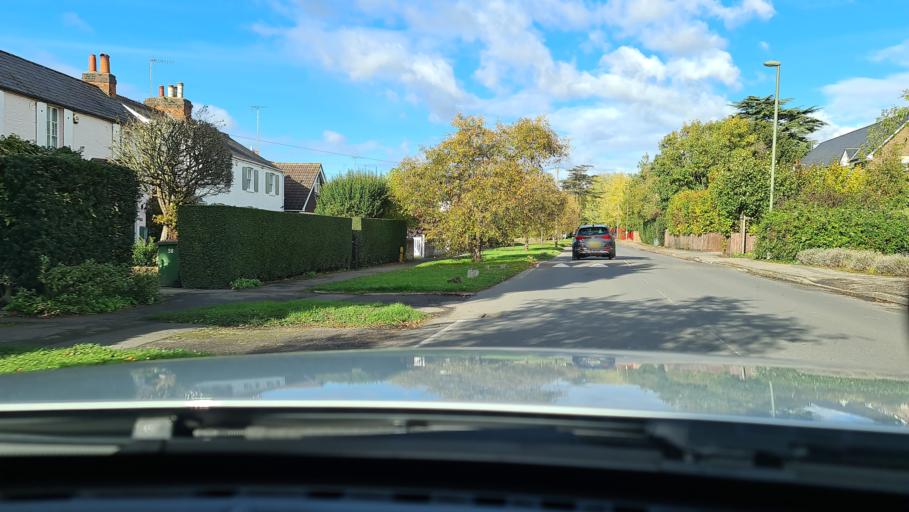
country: GB
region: England
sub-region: Surrey
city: Esher
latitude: 51.3638
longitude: -0.3789
